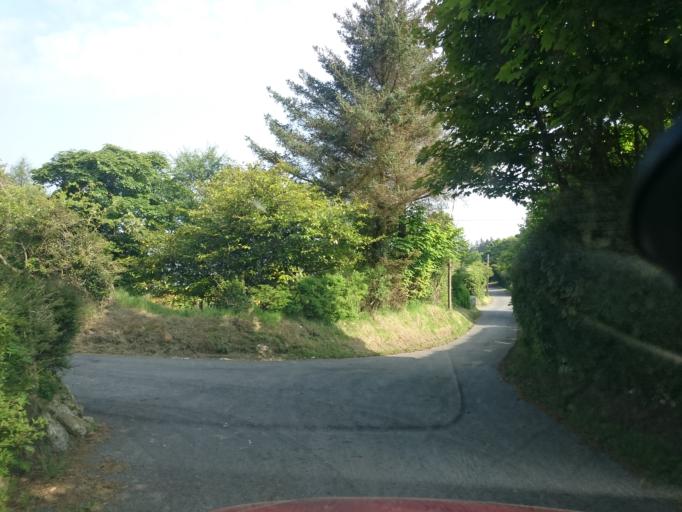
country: IE
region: Leinster
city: Ballinteer
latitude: 53.2515
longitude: -6.2517
